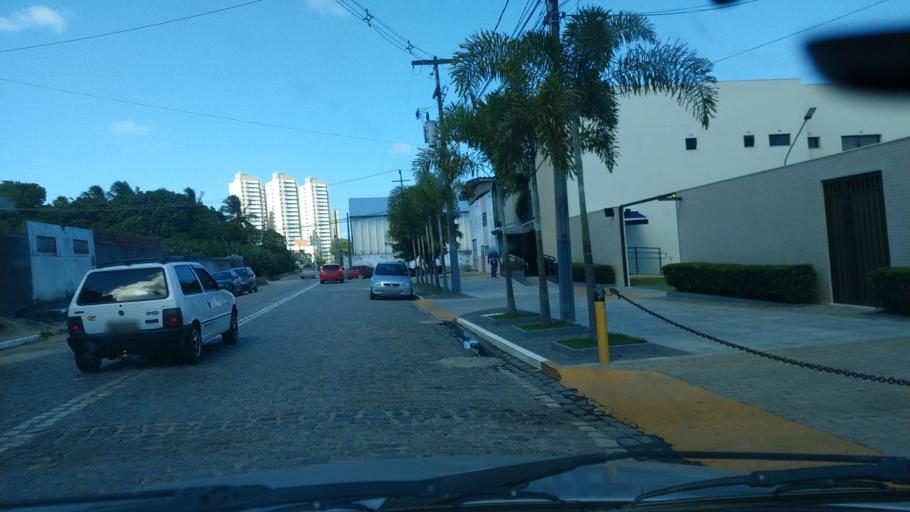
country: BR
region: Rio Grande do Norte
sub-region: Natal
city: Natal
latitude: -5.8582
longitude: -35.2145
